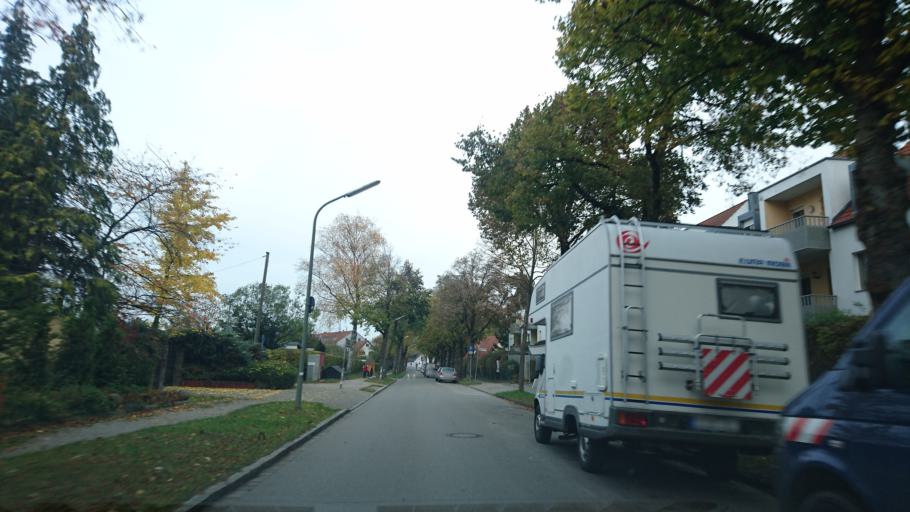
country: DE
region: Bavaria
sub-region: Swabia
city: Gersthofen
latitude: 48.3988
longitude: 10.8842
